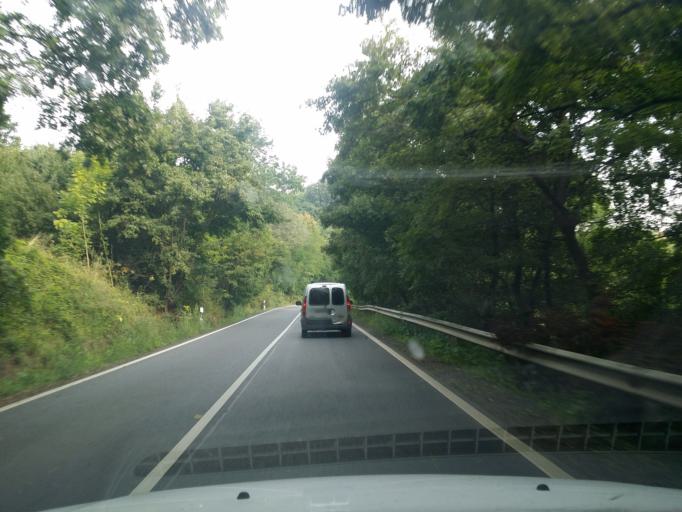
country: HU
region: Pest
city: Acsa
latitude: 47.7898
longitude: 19.3649
